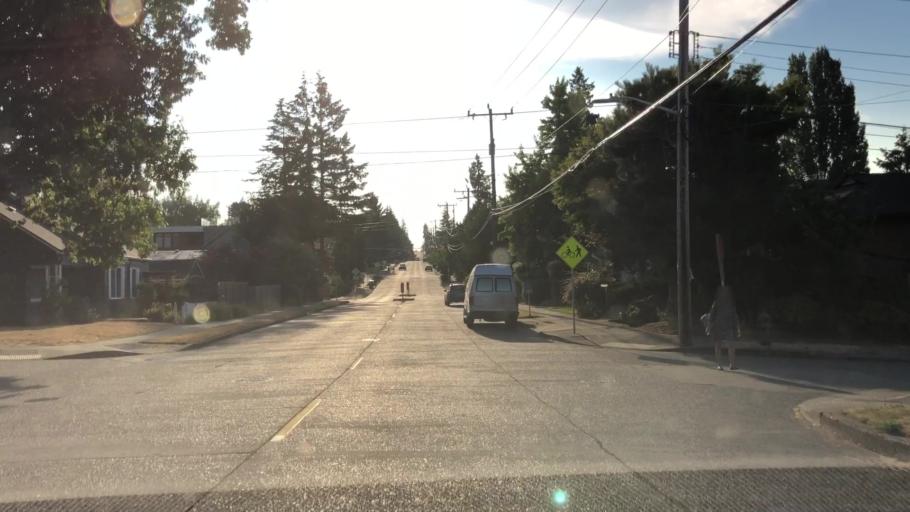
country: US
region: Washington
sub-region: King County
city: Inglewood-Finn Hill
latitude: 47.6794
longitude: -122.2874
